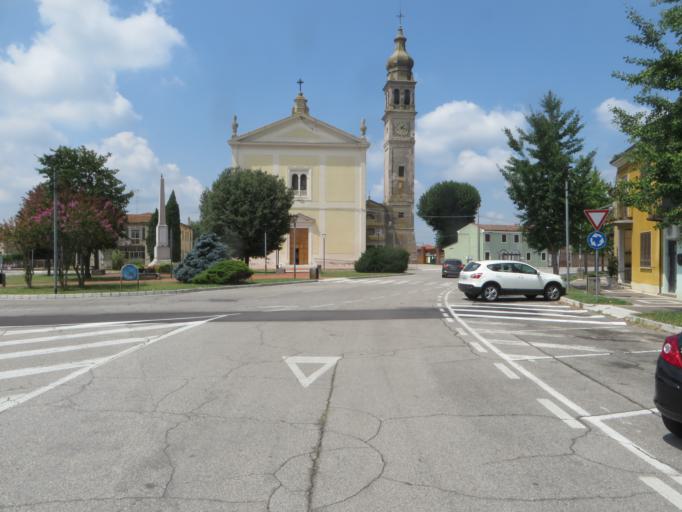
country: IT
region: Veneto
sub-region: Provincia di Verona
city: Angiari
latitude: 45.2181
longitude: 11.2844
